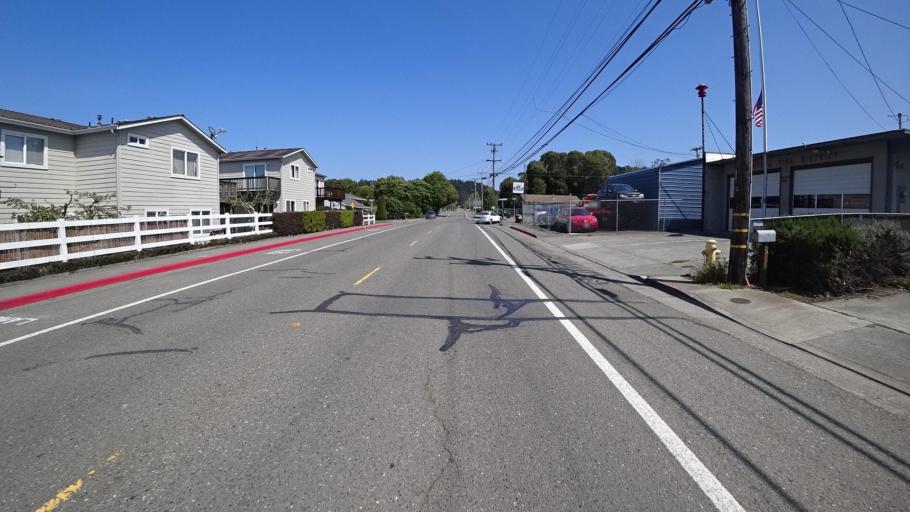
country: US
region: California
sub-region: Humboldt County
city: Fortuna
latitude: 40.5702
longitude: -124.1347
